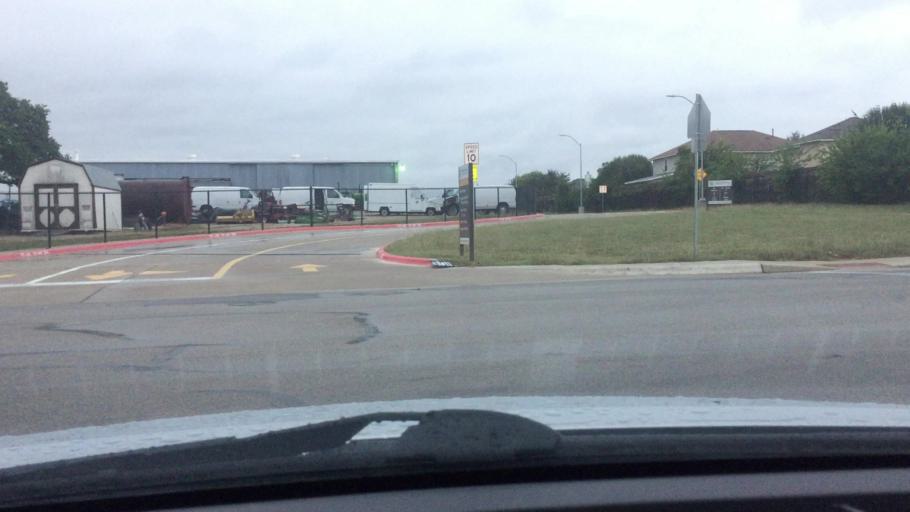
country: US
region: Texas
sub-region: Williamson County
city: Leander
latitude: 30.5774
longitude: -97.8572
